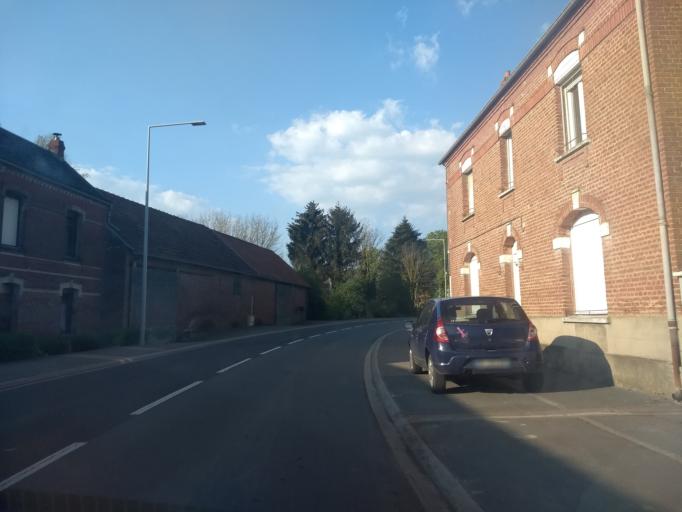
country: FR
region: Nord-Pas-de-Calais
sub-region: Departement du Pas-de-Calais
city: Bucquoy
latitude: 50.1353
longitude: 2.7070
